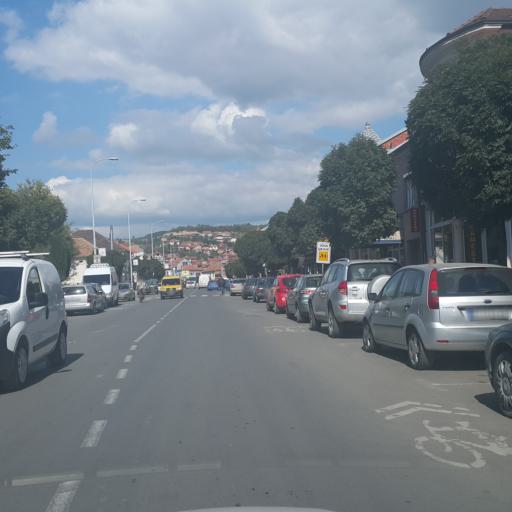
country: RS
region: Central Serbia
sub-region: Pirotski Okrug
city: Pirot
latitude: 43.1629
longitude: 22.5891
